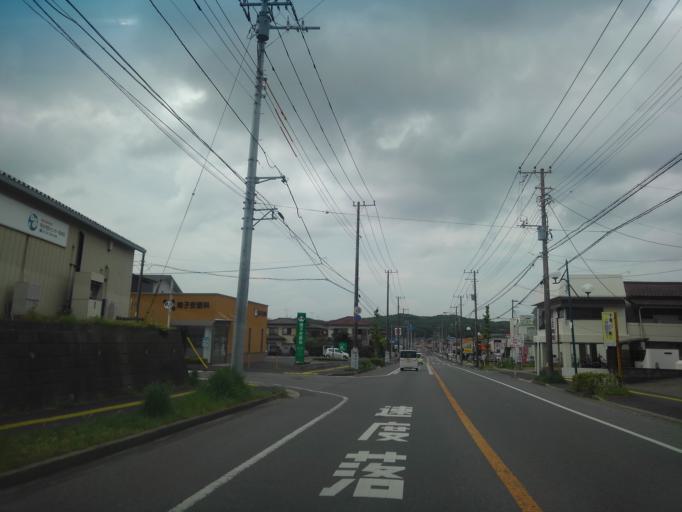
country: JP
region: Chiba
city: Kimitsu
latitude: 35.3299
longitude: 139.9197
